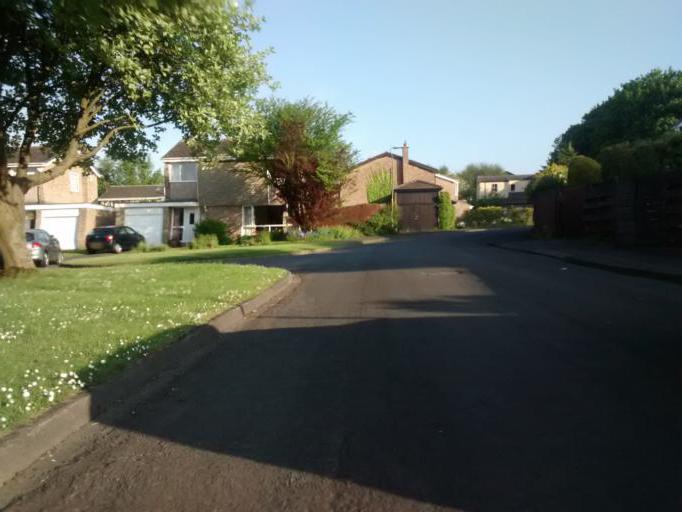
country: GB
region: England
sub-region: County Durham
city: Durham
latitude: 54.7522
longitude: -1.5386
